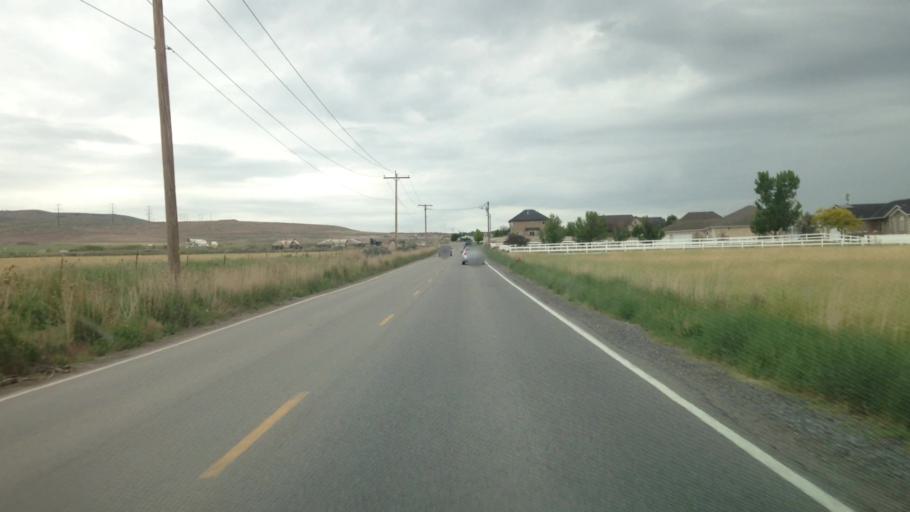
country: US
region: Utah
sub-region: Utah County
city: Saratoga Springs
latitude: 40.3886
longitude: -111.9354
